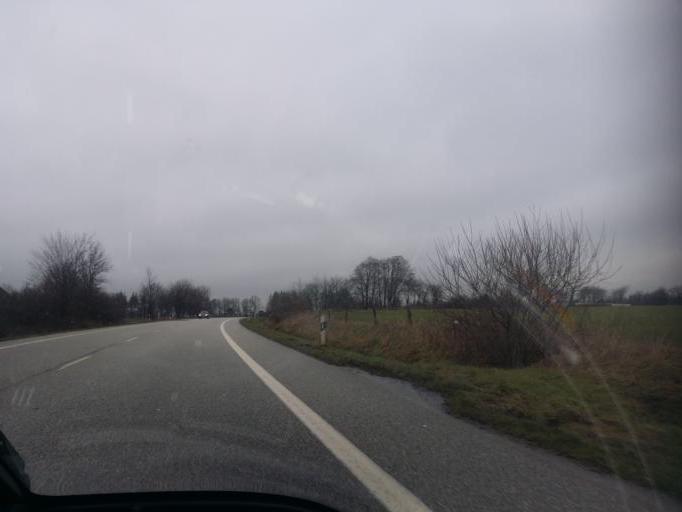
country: DE
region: Schleswig-Holstein
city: Bordelum
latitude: 54.6439
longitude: 8.9465
